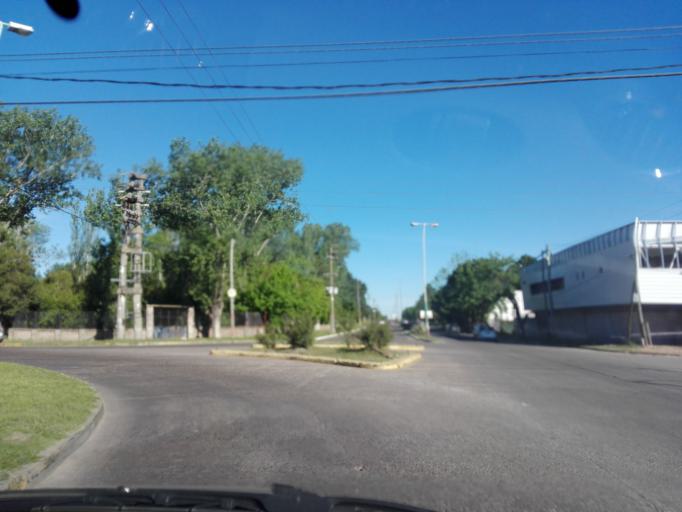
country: AR
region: Buenos Aires
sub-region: Partido de La Plata
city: La Plata
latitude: -34.8966
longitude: -58.0017
